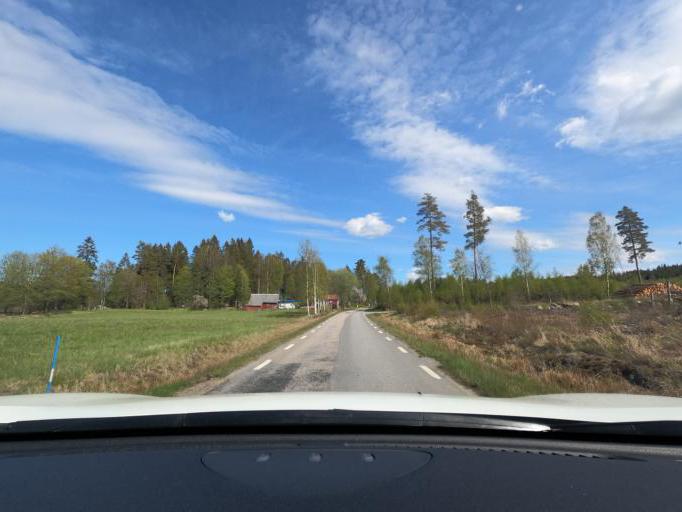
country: SE
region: Vaestra Goetaland
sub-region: Marks Kommun
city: Horred
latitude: 57.4512
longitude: 12.4522
